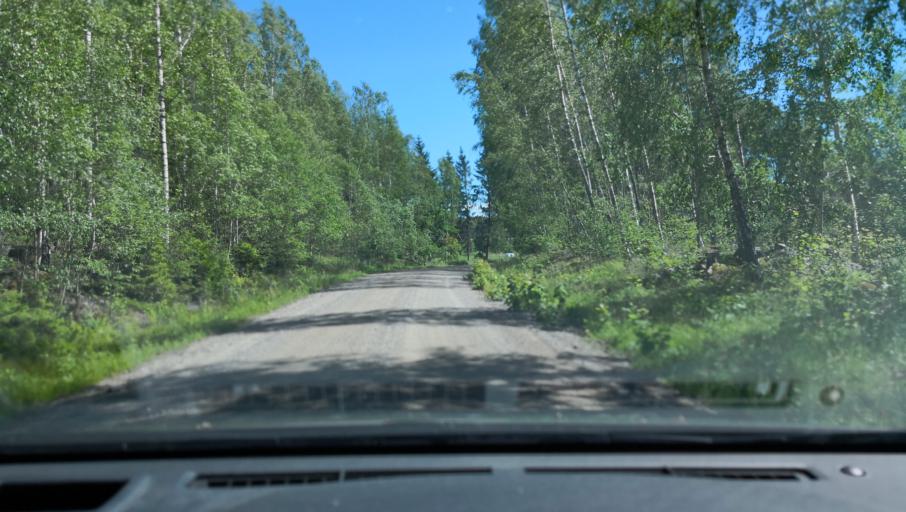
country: SE
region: Vaestmanland
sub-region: Arboga Kommun
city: Tyringe
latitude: 59.3280
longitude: 15.9750
